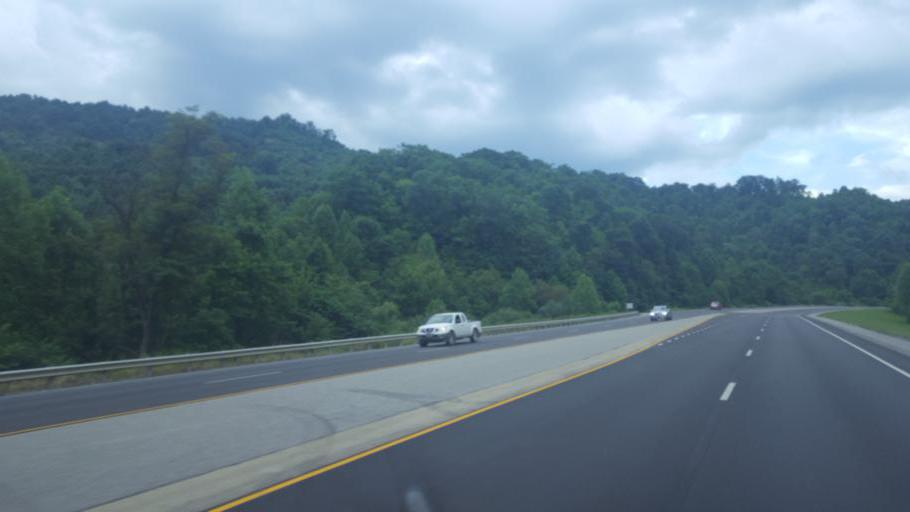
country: US
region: Kentucky
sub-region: Letcher County
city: Jenkins
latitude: 37.2952
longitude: -82.5469
